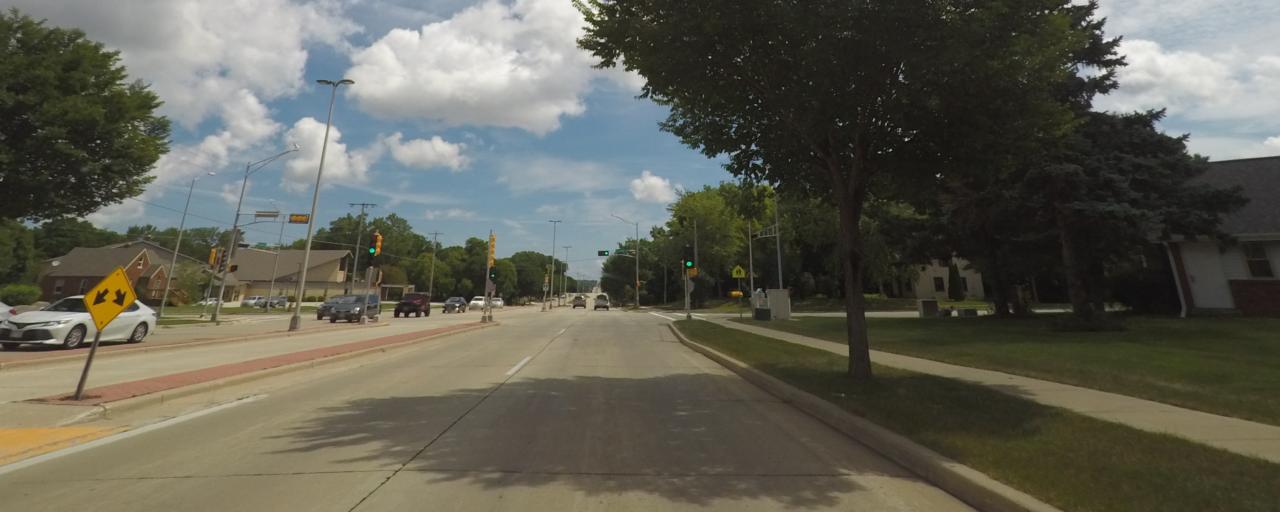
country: US
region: Wisconsin
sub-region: Milwaukee County
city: Hales Corners
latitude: 42.9590
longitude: -88.0586
